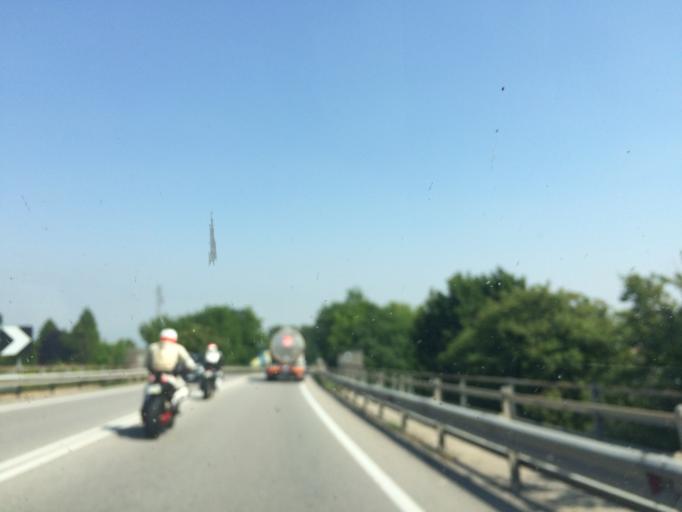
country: IT
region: Veneto
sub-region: Provincia di Padova
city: Cittadella
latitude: 45.6365
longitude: 11.7757
